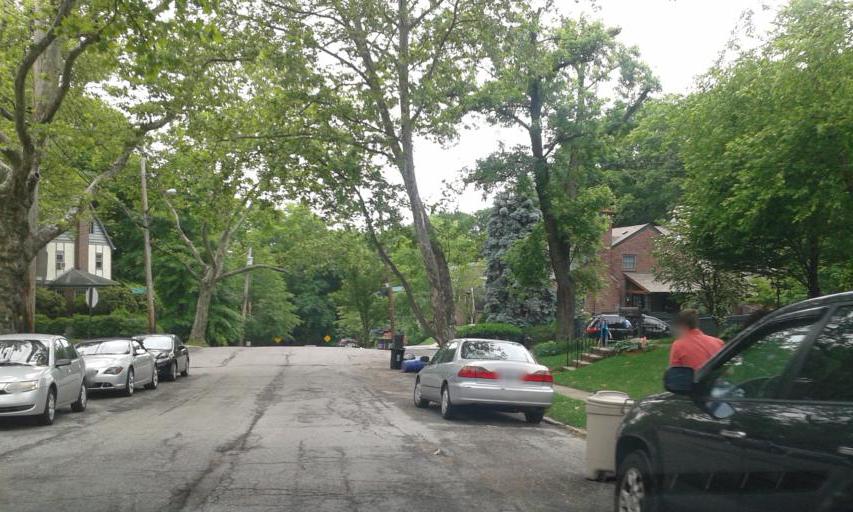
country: US
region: New Jersey
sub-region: Hudson County
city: Bayonne
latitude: 40.6344
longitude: -74.0994
